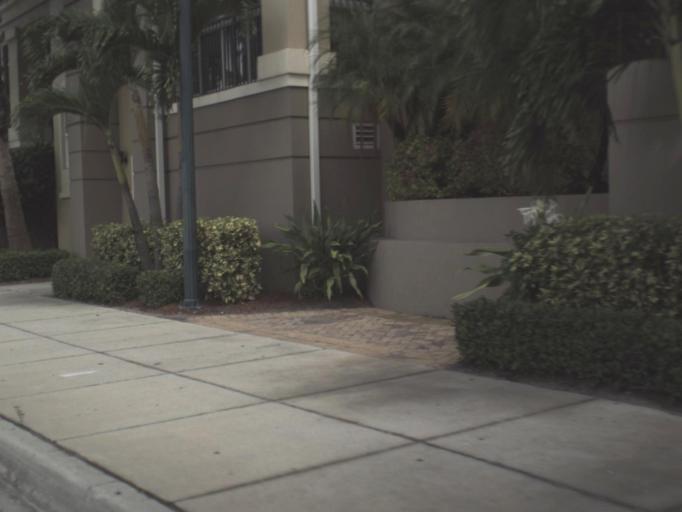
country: US
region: Florida
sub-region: Sarasota County
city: Sarasota
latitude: 27.3465
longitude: -82.5468
